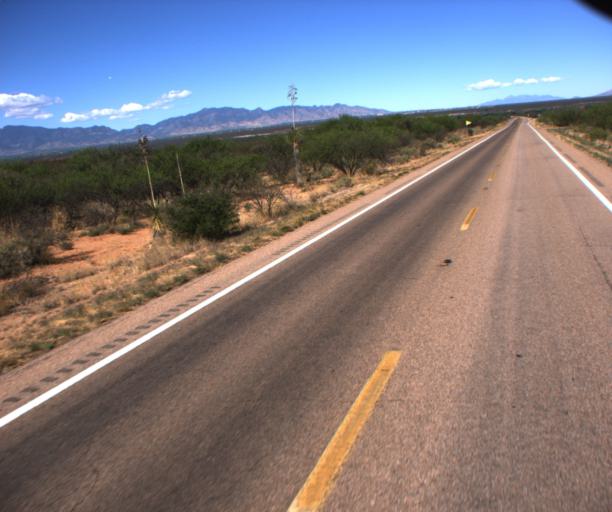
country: US
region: Arizona
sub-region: Cochise County
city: Sierra Vista Southeast
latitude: 31.5503
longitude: -110.1113
